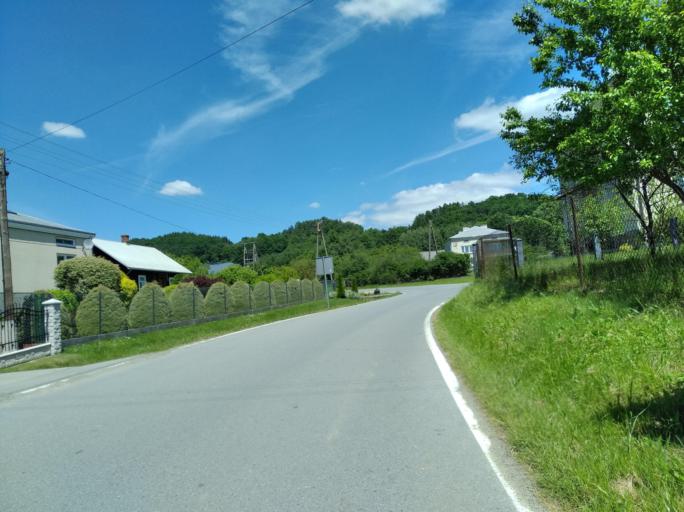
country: PL
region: Subcarpathian Voivodeship
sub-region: Powiat krosnienski
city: Wojaszowka
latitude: 49.7879
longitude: 21.6909
